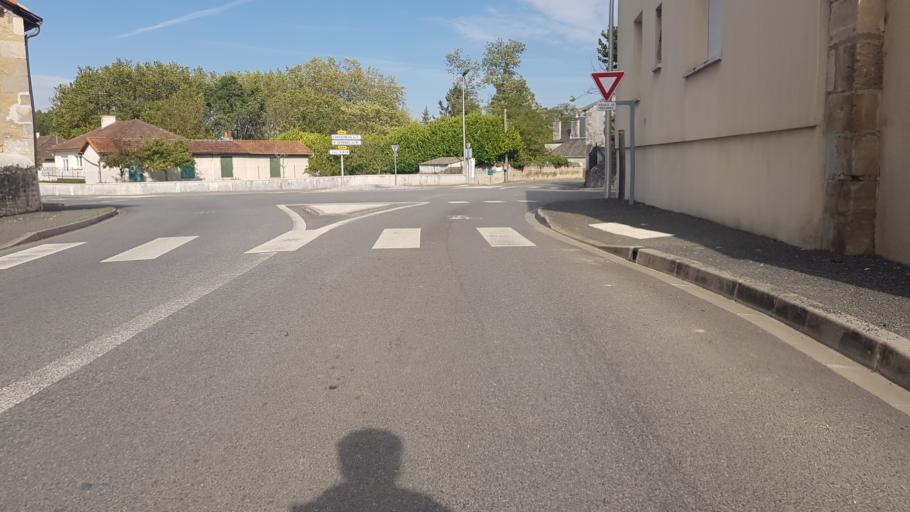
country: FR
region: Poitou-Charentes
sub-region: Departement de la Vienne
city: Chasseneuil-du-Poitou
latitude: 46.6308
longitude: 0.3695
